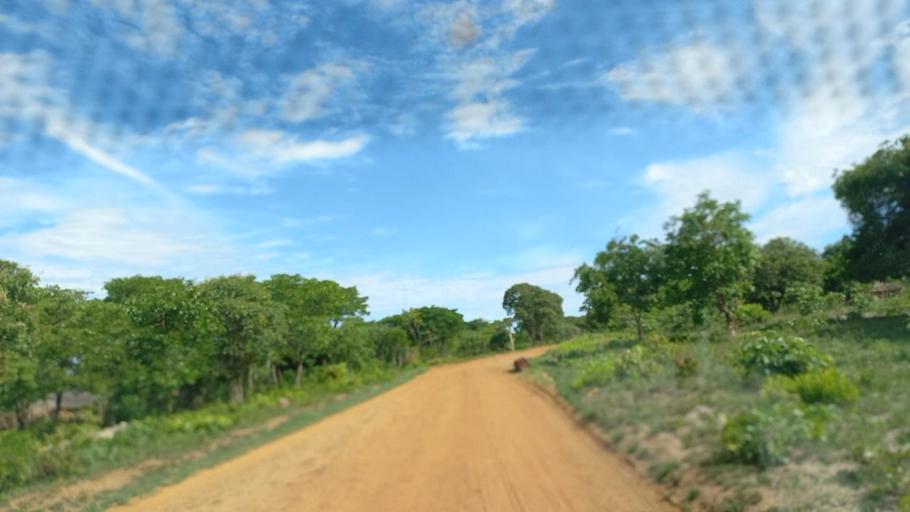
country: ZM
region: North-Western
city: Kabompo
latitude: -13.0726
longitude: 24.2181
